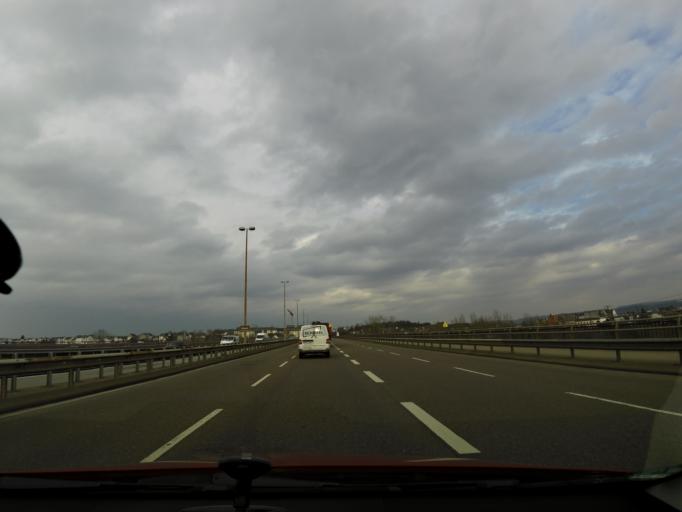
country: DE
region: Rheinland-Pfalz
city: Koblenz
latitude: 50.3629
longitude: 7.5881
